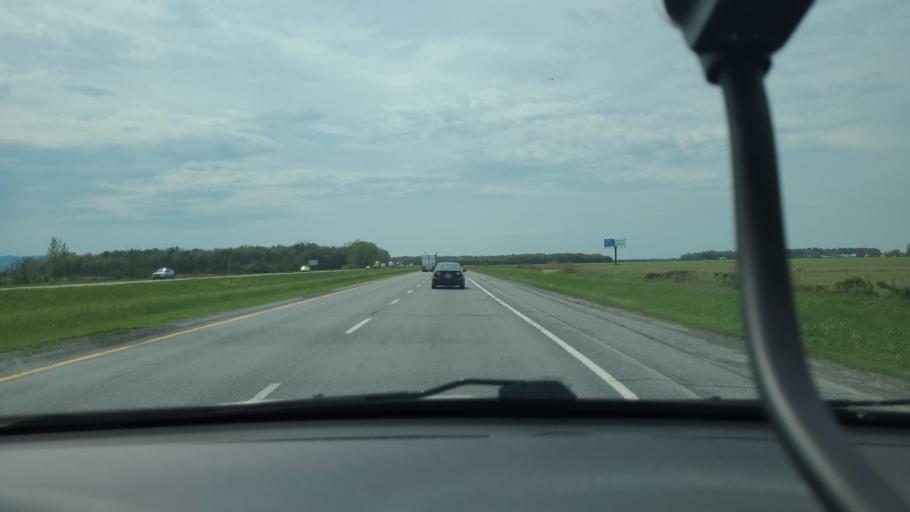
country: CA
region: Quebec
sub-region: Monteregie
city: Saint-Hyacinthe
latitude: 45.6334
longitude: -73.0094
